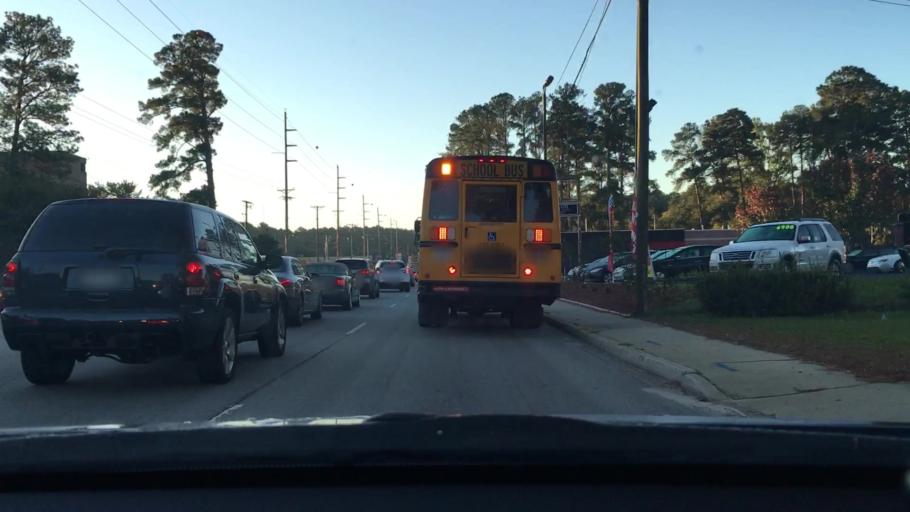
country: US
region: South Carolina
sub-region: Lexington County
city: Saint Andrews
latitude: 34.0676
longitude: -81.1179
